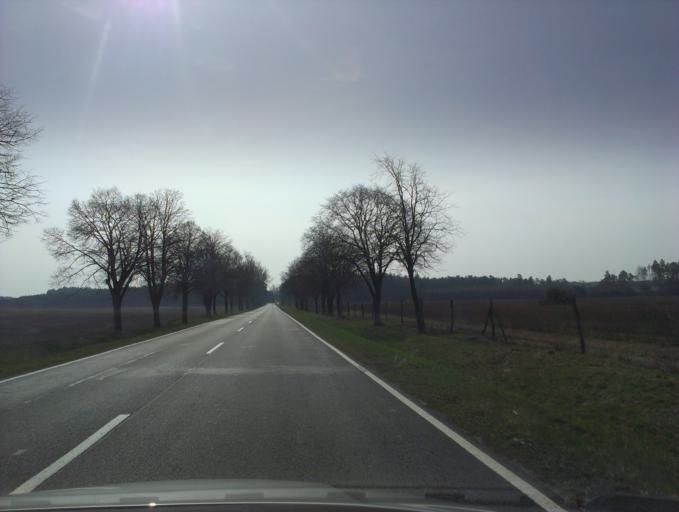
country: PL
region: Greater Poland Voivodeship
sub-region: Powiat zlotowski
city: Okonek
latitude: 53.5573
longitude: 16.8363
